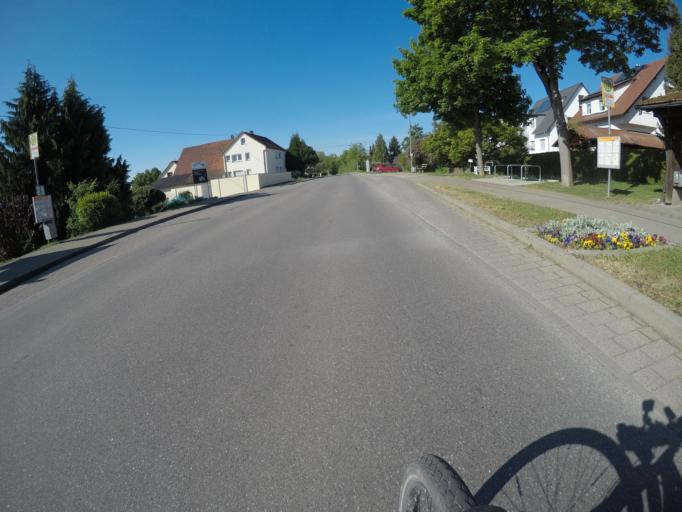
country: DE
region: Baden-Wuerttemberg
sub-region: Regierungsbezirk Stuttgart
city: Altenriet
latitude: 48.5951
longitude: 9.1957
